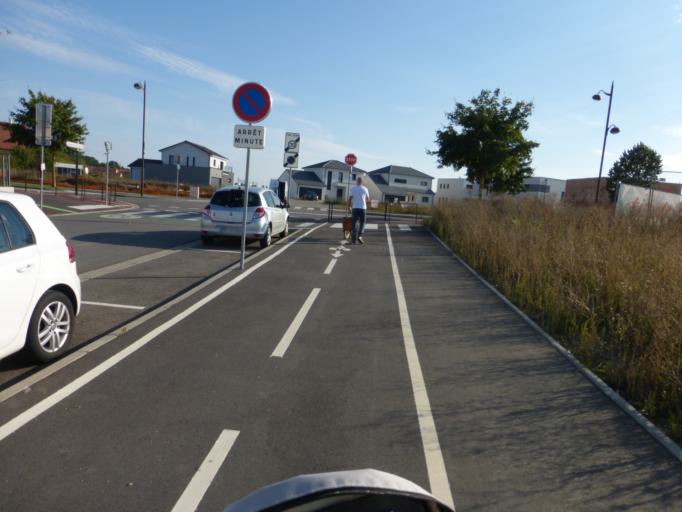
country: FR
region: Lorraine
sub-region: Departement de Meurthe-et-Moselle
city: Pulnoy
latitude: 48.6998
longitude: 6.2510
